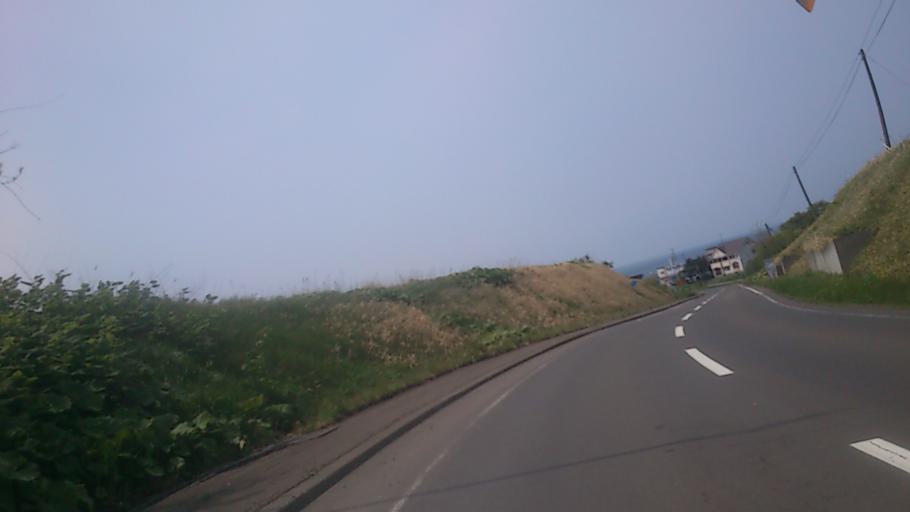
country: JP
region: Hokkaido
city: Nemuro
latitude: 43.2792
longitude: 145.5095
